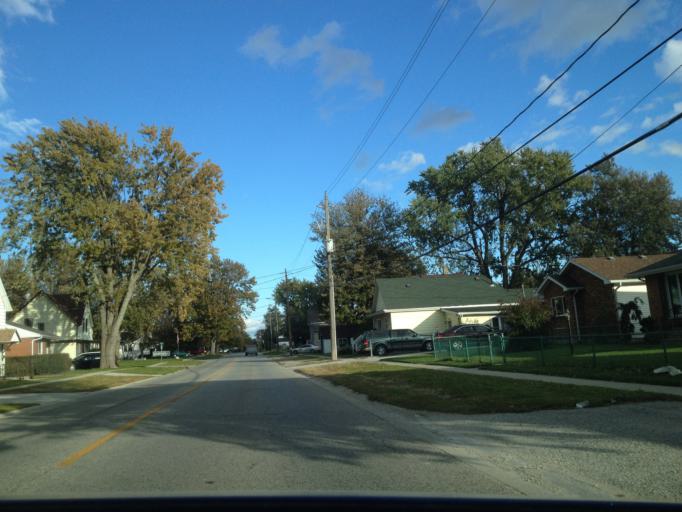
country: US
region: Michigan
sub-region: Wayne County
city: Grosse Pointe Farms
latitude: 42.2939
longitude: -82.7084
